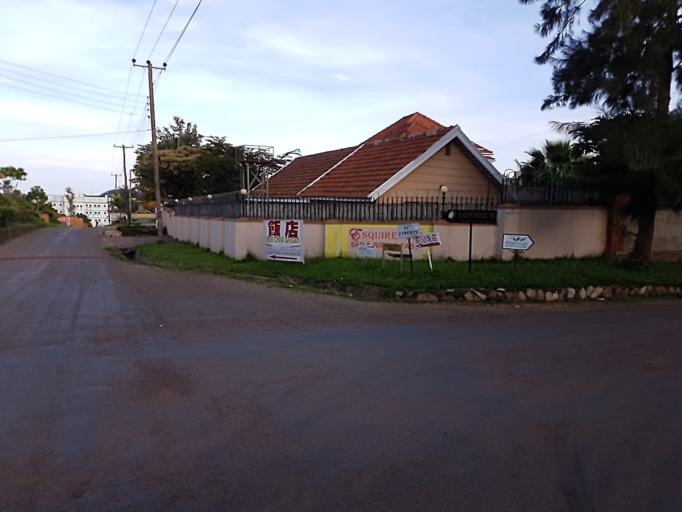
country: UG
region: Central Region
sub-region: Wakiso District
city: Entebbe
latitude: 0.0476
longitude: 32.4677
